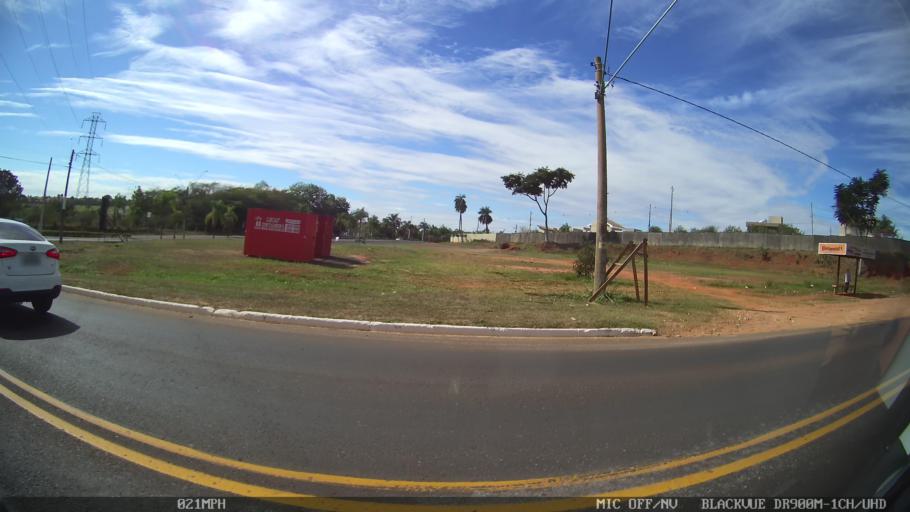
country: BR
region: Sao Paulo
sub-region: Sao Jose Do Rio Preto
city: Sao Jose do Rio Preto
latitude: -20.8287
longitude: -49.3429
